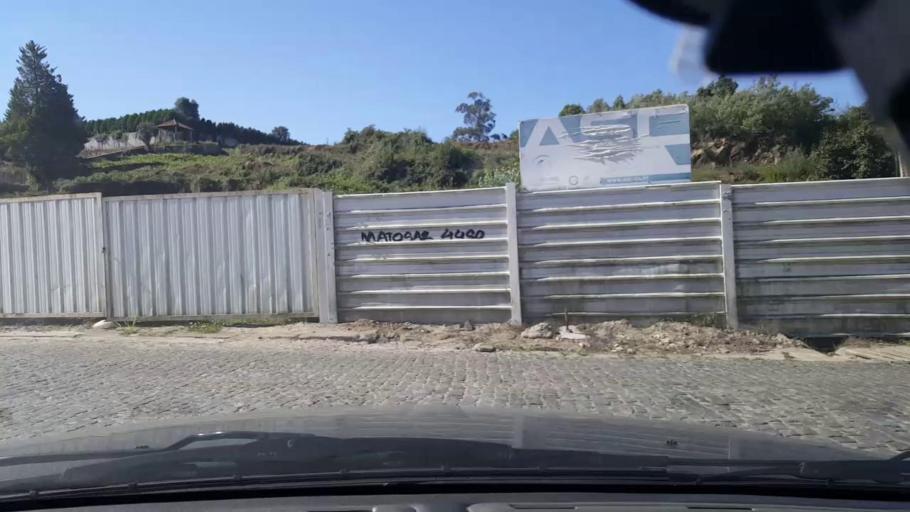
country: PT
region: Porto
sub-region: Maia
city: Gemunde
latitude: 41.2786
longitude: -8.6714
